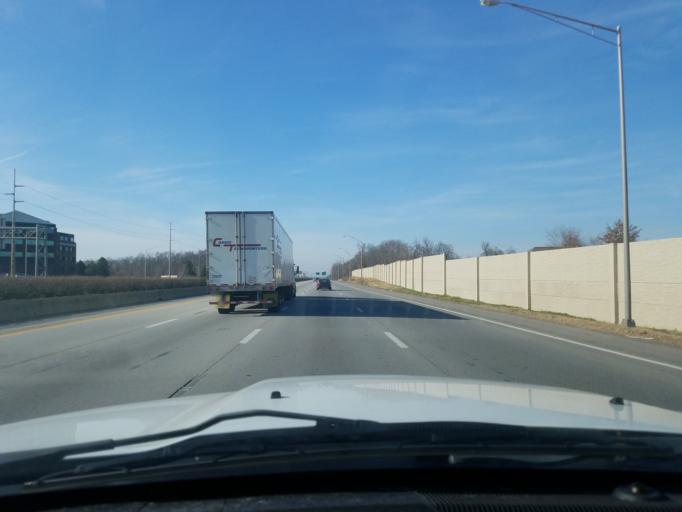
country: US
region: Kentucky
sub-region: Jefferson County
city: Hurstbourne Acres
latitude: 38.2257
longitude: -85.5853
